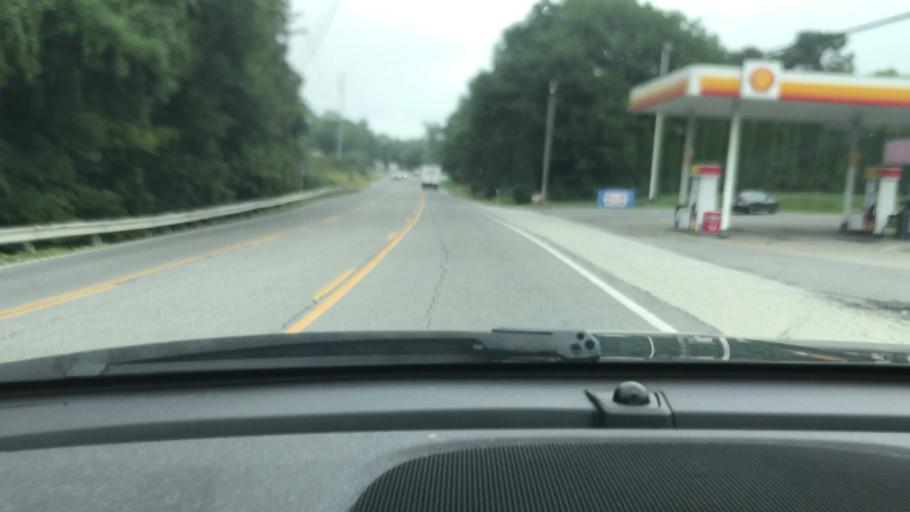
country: US
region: Tennessee
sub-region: Sumner County
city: Millersville
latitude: 36.4070
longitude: -86.6874
